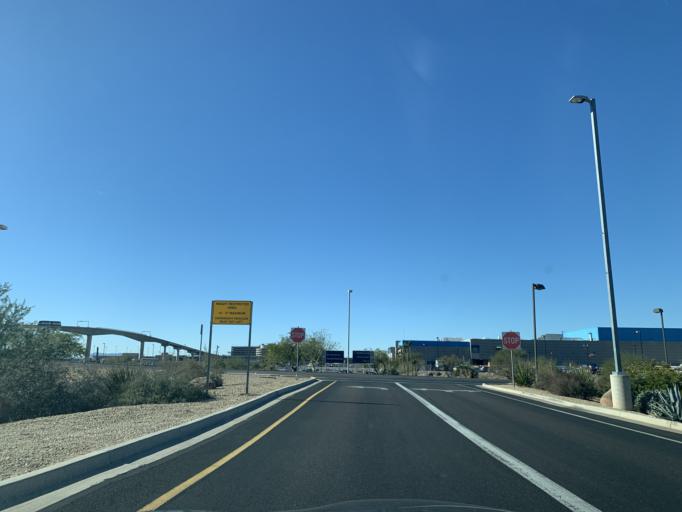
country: US
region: Arizona
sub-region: Maricopa County
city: Tempe Junction
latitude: 33.4369
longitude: -111.9874
